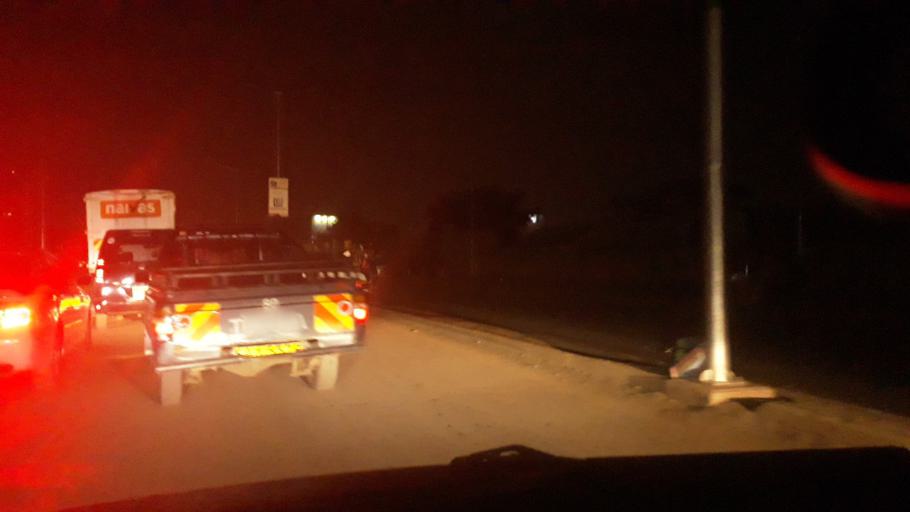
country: KE
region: Nairobi Area
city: Pumwani
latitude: -1.3110
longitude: 36.8561
